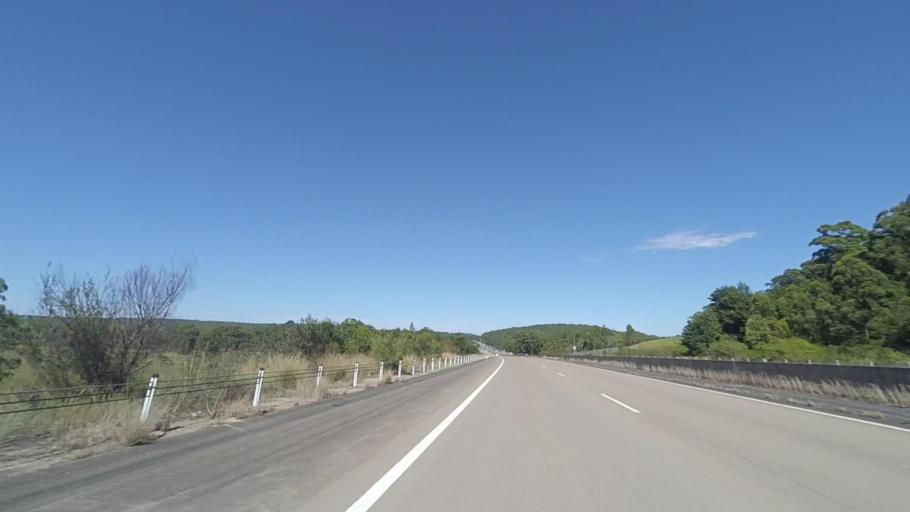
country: AU
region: New South Wales
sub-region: Port Stephens Shire
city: Port Stephens
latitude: -32.6206
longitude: 151.9673
